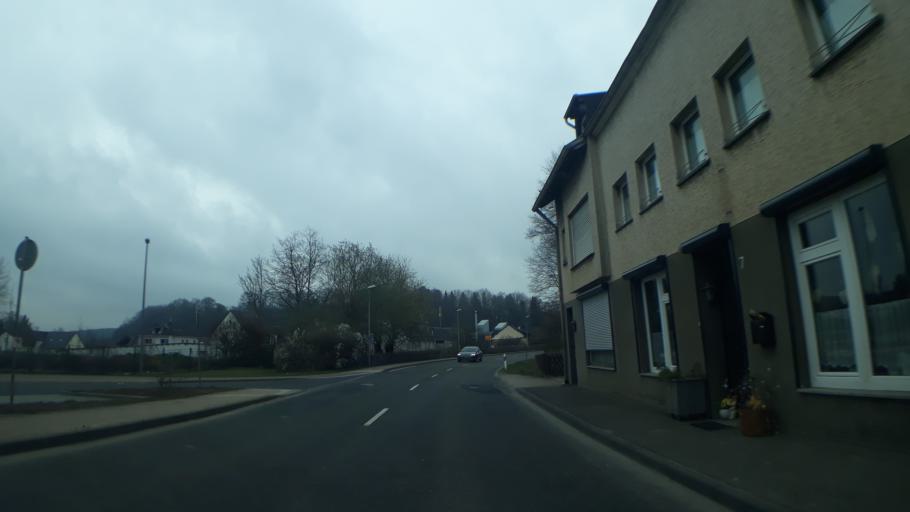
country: DE
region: North Rhine-Westphalia
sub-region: Regierungsbezirk Koln
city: Kall
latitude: 50.5394
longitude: 6.5586
